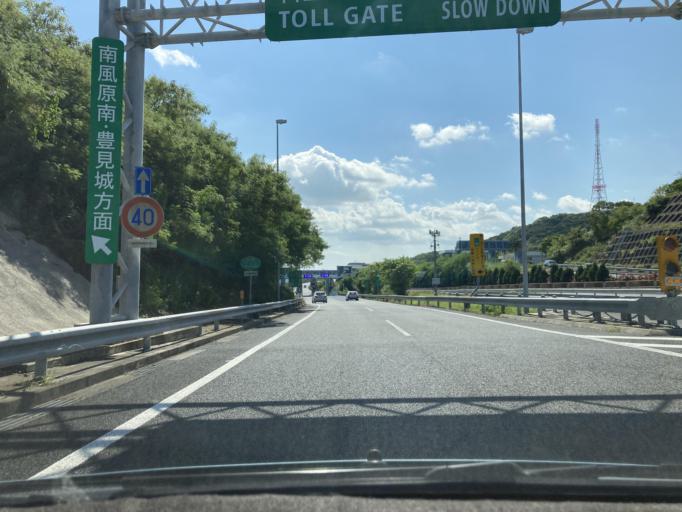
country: JP
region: Okinawa
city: Ginowan
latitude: 26.2232
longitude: 127.7384
